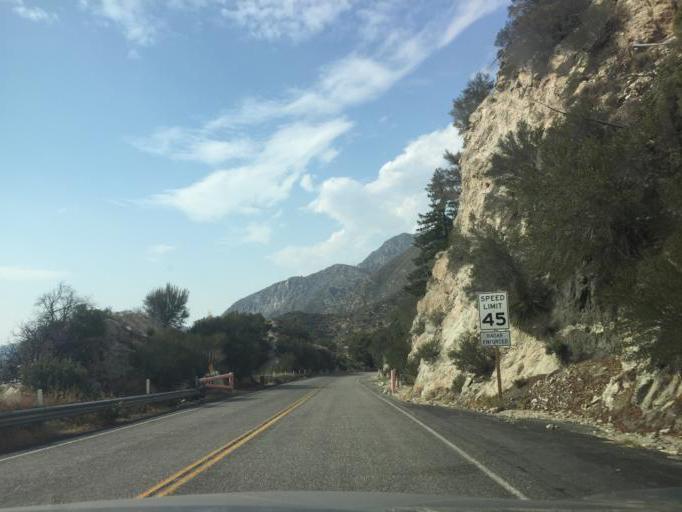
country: US
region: California
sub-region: Los Angeles County
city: Altadena
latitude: 34.2601
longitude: -118.1070
